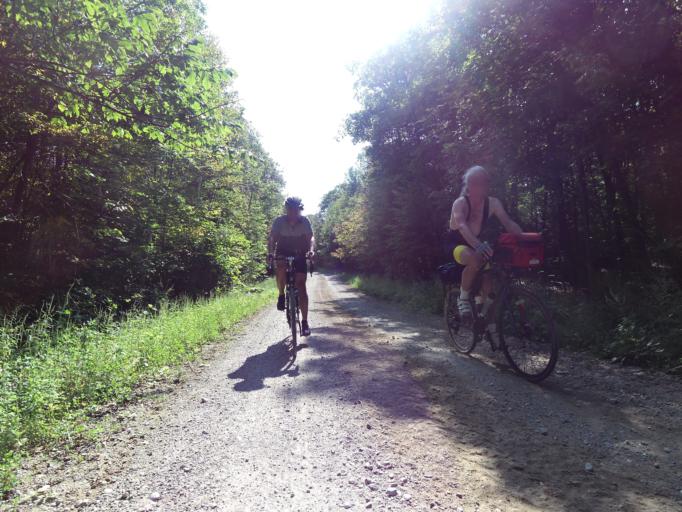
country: CA
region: Ontario
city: Perth
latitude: 45.0193
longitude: -76.6153
